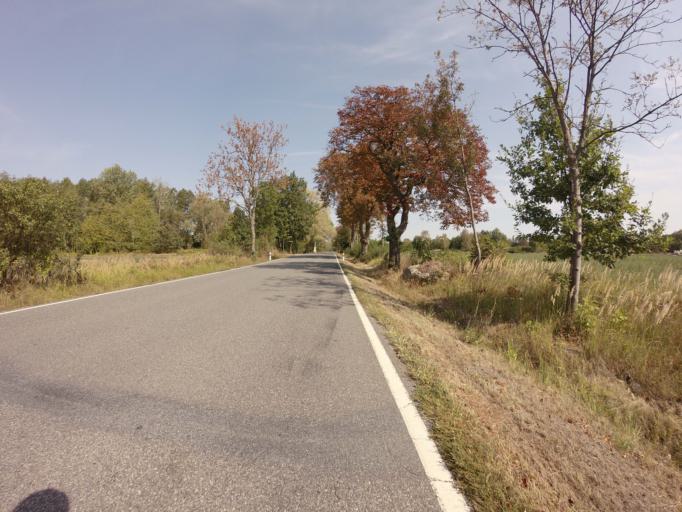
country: CZ
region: Central Bohemia
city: Sedlcany
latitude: 49.6062
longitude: 14.3843
